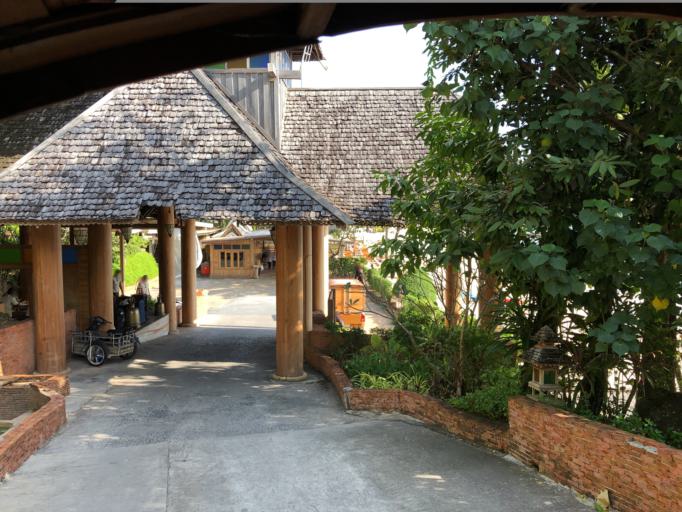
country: TH
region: Phangnga
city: Ban Phru Nai
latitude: 7.9828
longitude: 98.5680
